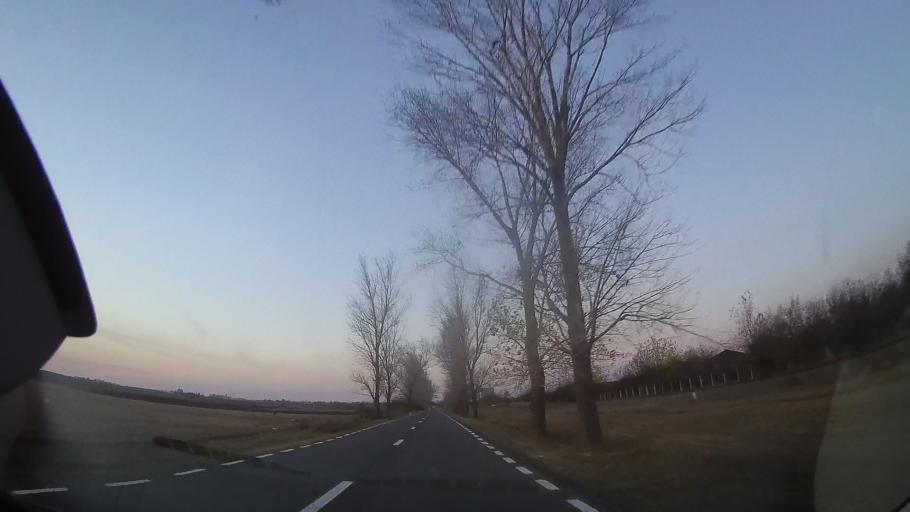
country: RO
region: Constanta
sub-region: Comuna Cobadin
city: Cobadin
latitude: 44.0447
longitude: 28.2536
